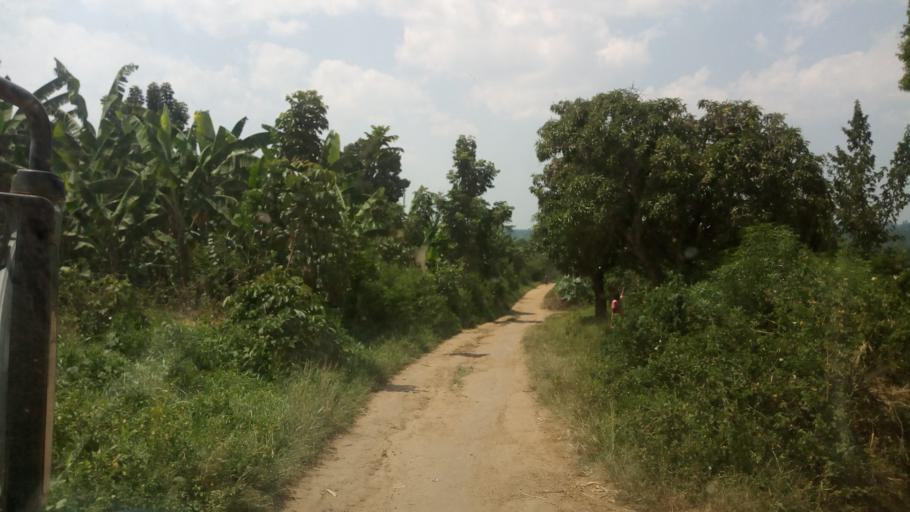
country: UG
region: Western Region
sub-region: Kanungu District
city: Ntungamo
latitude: -0.7783
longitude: 29.6510
